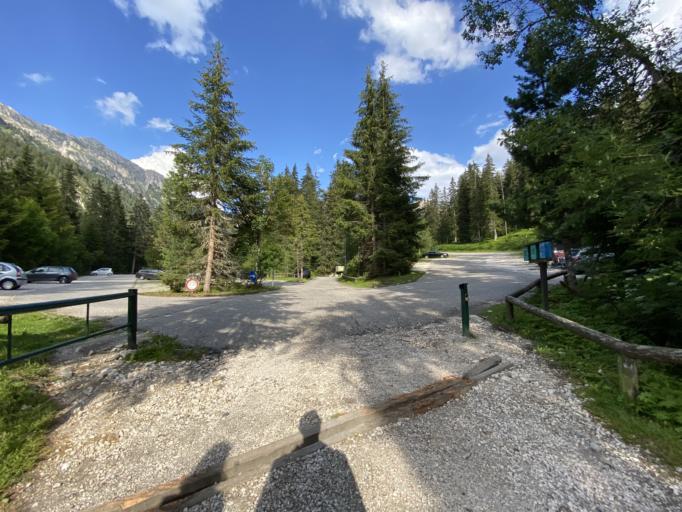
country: IT
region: Trentino-Alto Adige
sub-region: Bolzano
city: Santa Cristina Valgardena
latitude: 46.6351
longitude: 11.7624
